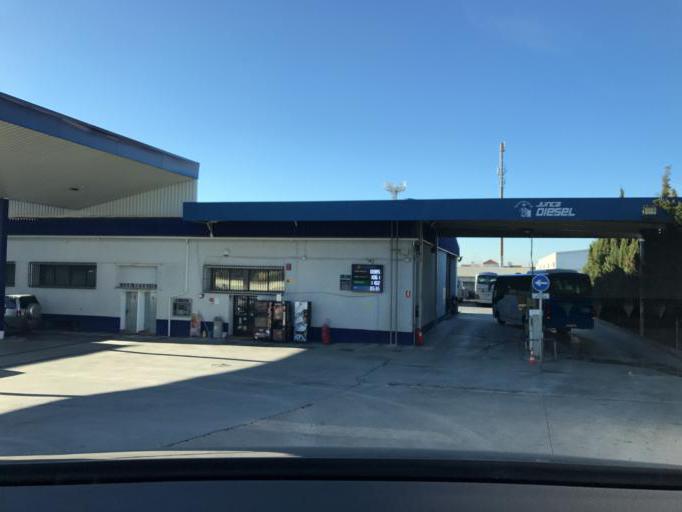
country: ES
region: Andalusia
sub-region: Provincia de Granada
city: Albolote
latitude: 37.2310
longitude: -3.6473
